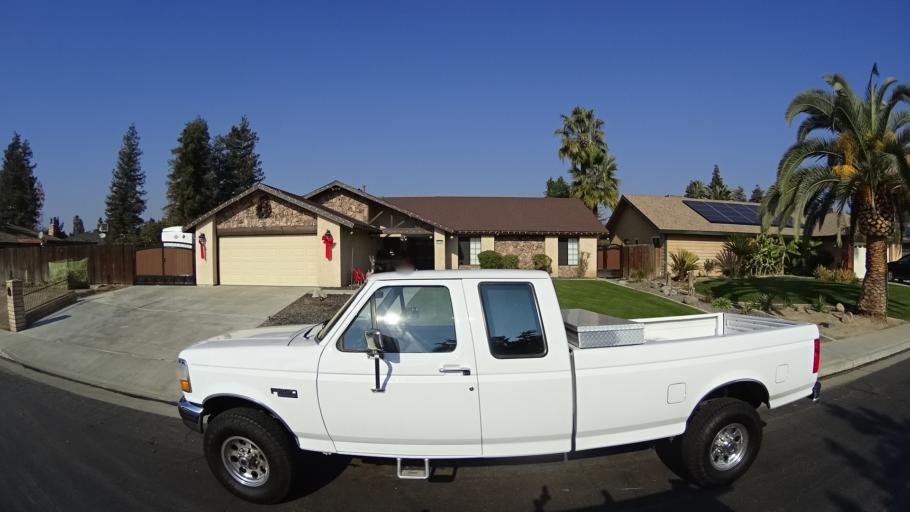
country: US
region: California
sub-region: Kern County
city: Greenacres
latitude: 35.3248
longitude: -119.0778
